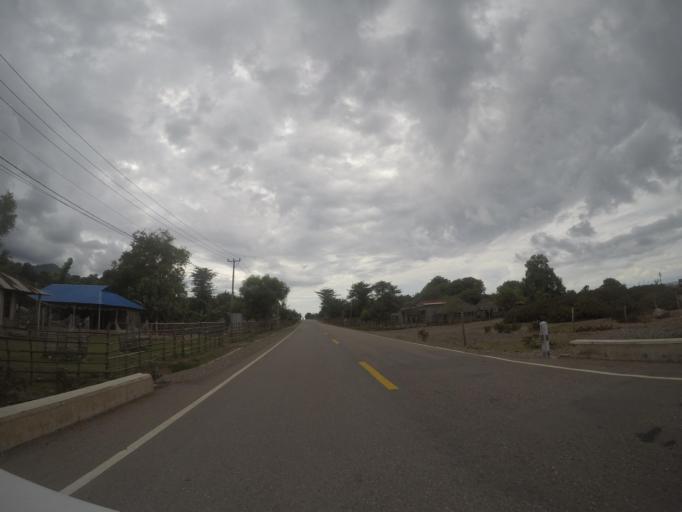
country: TL
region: Bobonaro
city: Maliana
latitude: -8.8279
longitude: 125.0683
